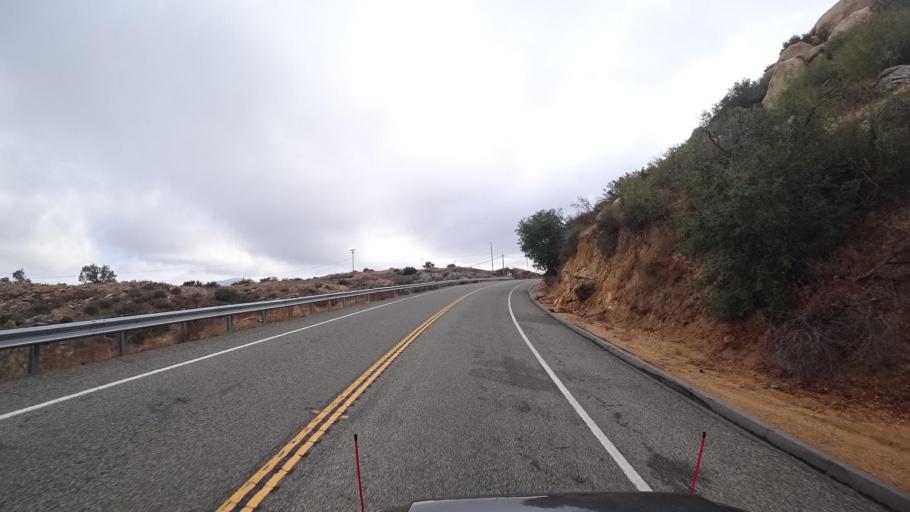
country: MX
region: Baja California
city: Tecate
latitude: 32.6013
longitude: -116.5938
